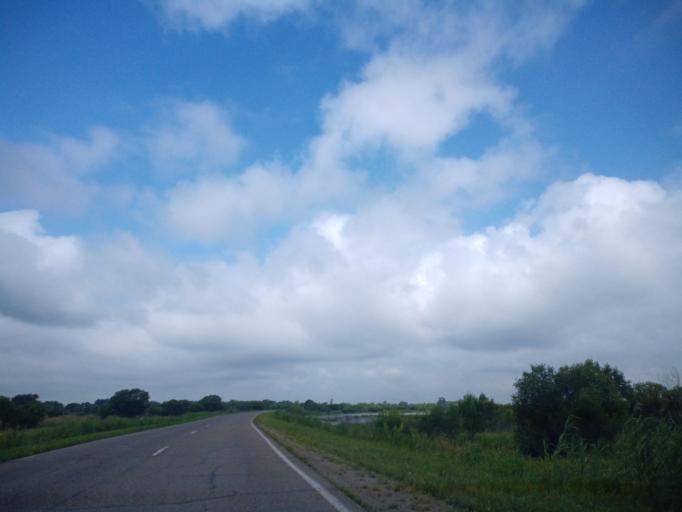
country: RU
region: Primorskiy
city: Dal'nerechensk
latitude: 45.9339
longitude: 133.8343
